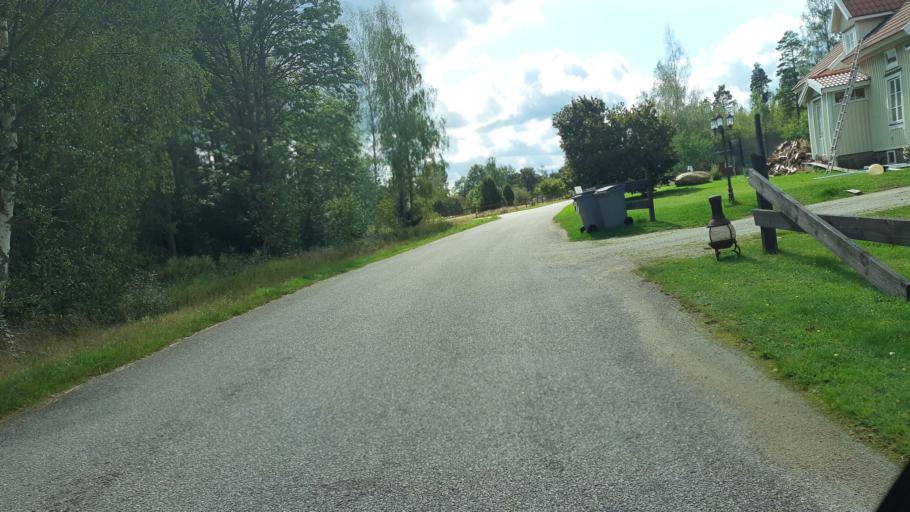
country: SE
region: Kronoberg
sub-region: Tingsryds Kommun
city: Tingsryd
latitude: 56.4591
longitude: 15.1583
